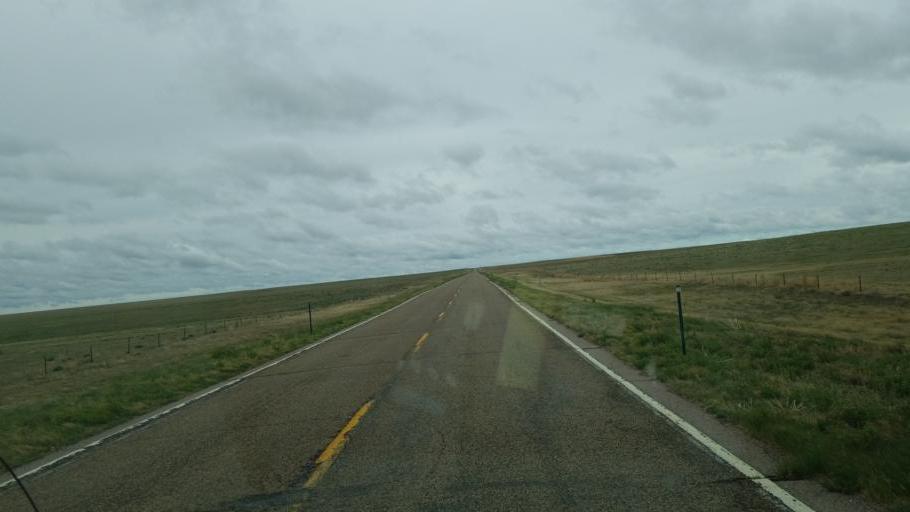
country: US
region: Colorado
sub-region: Lincoln County
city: Hugo
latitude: 38.8501
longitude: -103.4262
